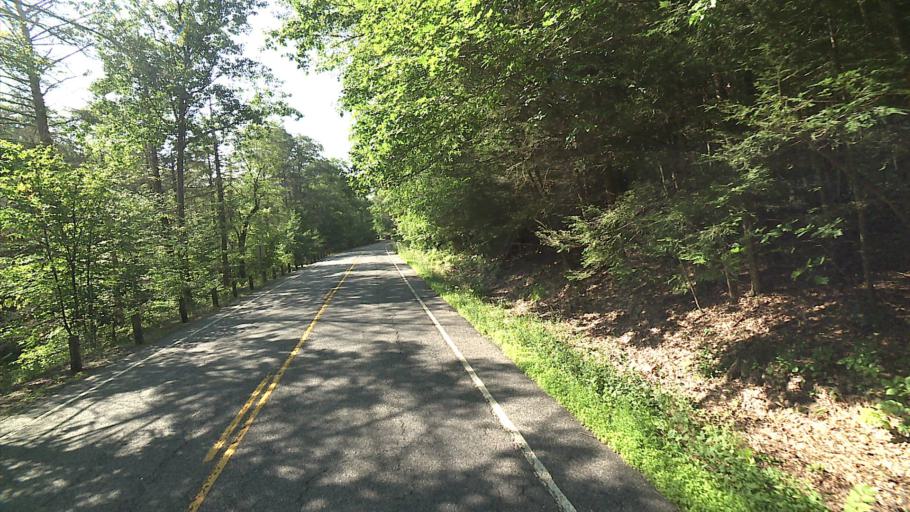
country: US
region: Connecticut
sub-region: Litchfield County
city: Winsted
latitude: 42.0245
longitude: -73.1187
